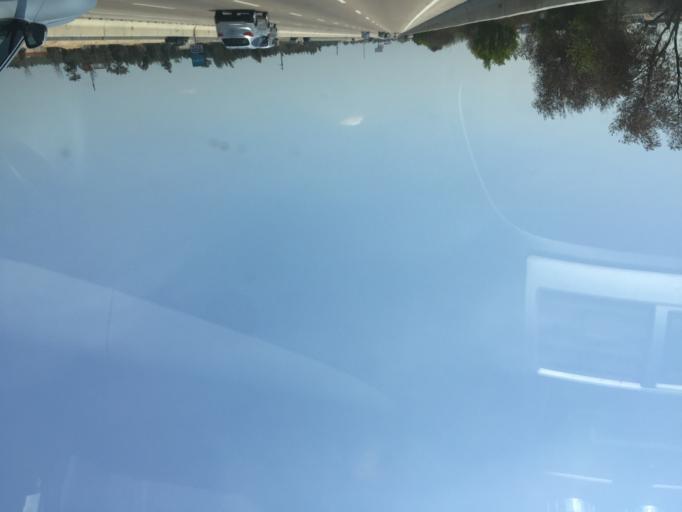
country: EG
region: Al Buhayrah
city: Beheira
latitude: 30.4302
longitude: 30.3394
